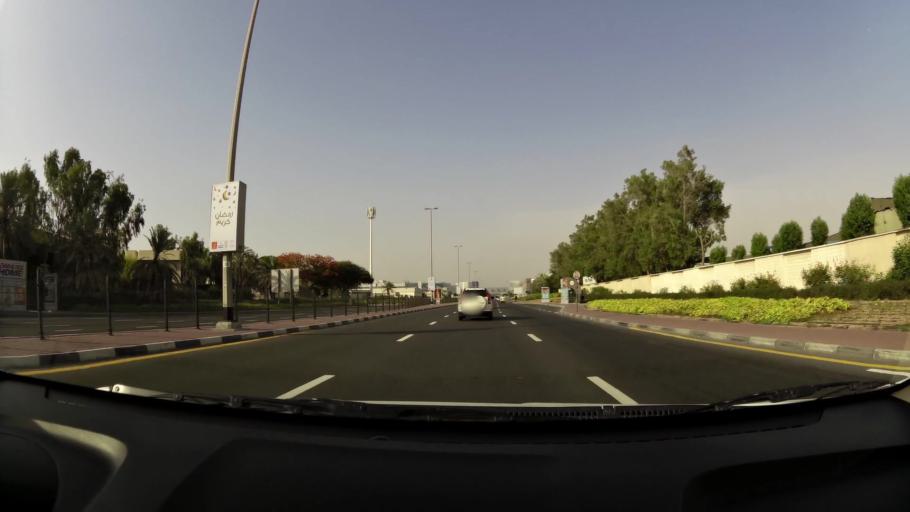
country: AE
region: Ash Shariqah
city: Sharjah
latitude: 25.2342
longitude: 55.3593
